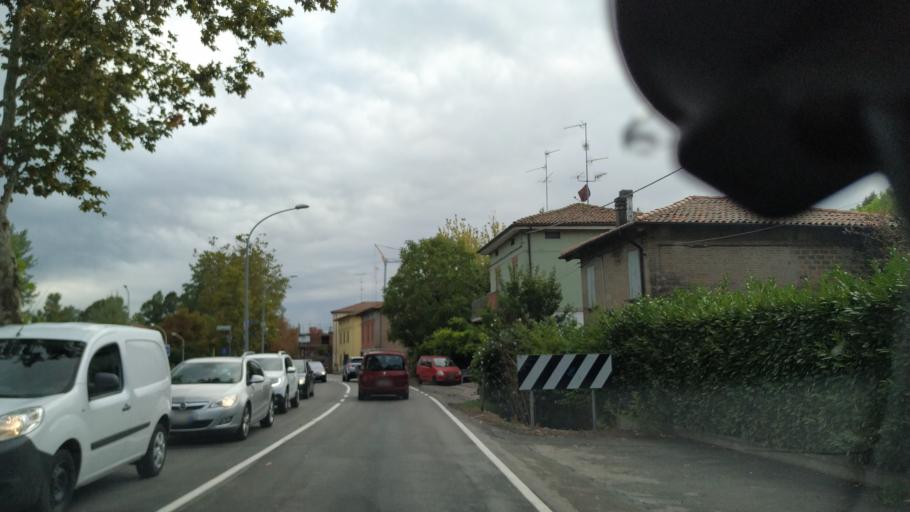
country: IT
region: Emilia-Romagna
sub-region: Provincia di Bologna
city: Decima
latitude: 44.7117
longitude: 11.2325
